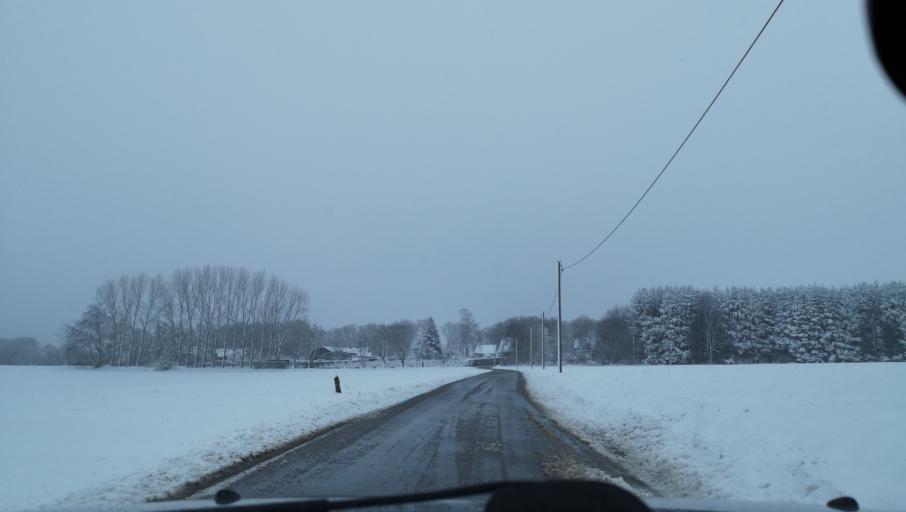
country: DE
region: North Rhine-Westphalia
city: Radevormwald
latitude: 51.2338
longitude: 7.3619
